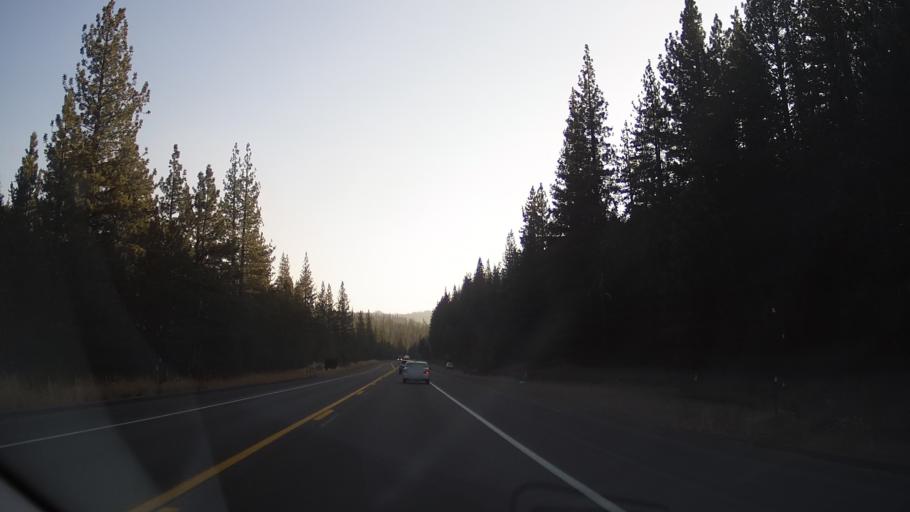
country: US
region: California
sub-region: Nevada County
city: Truckee
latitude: 39.3058
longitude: -120.2060
